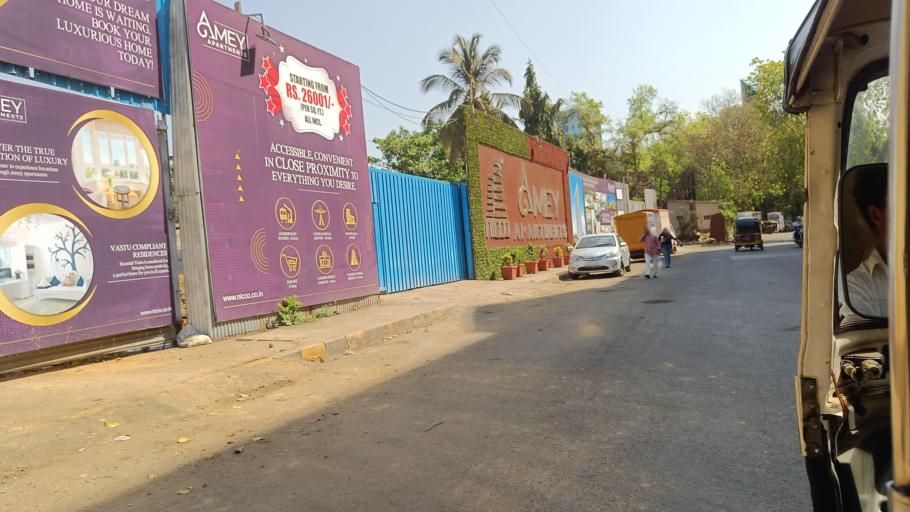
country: IN
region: Maharashtra
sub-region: Mumbai Suburban
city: Powai
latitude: 19.1245
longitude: 72.8549
